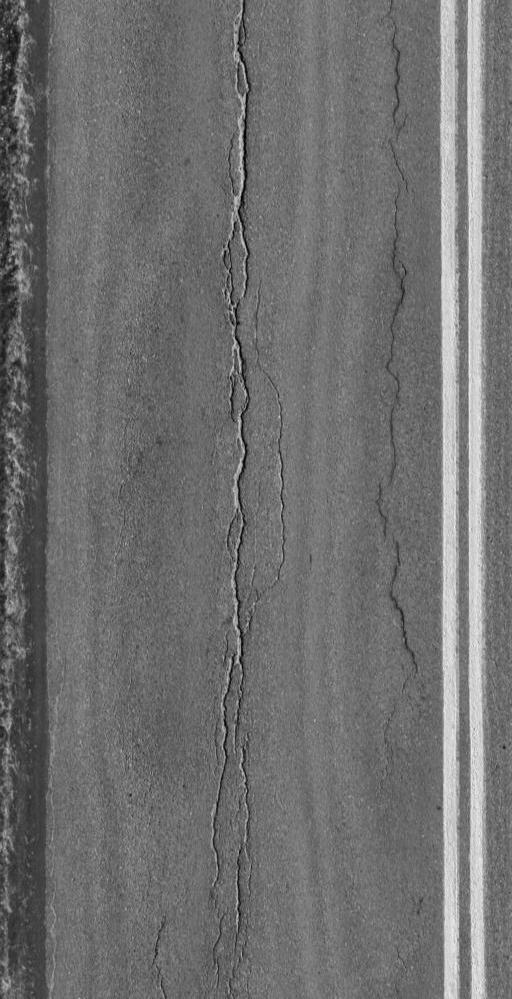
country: US
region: Vermont
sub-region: Chittenden County
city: Hinesburg
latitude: 44.3342
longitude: -73.1925
